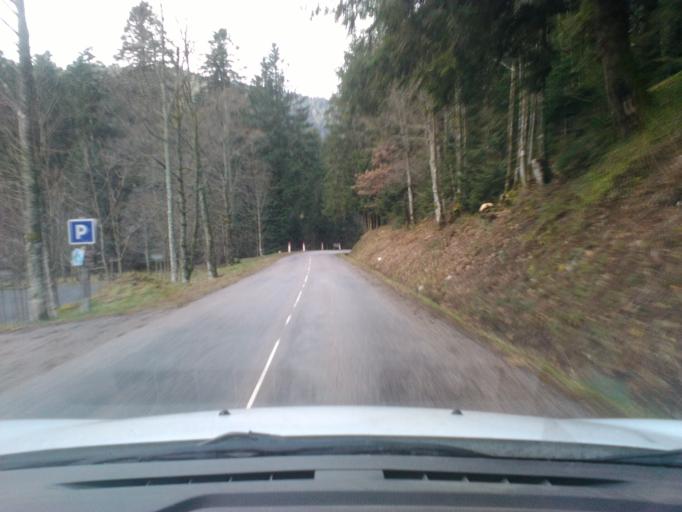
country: FR
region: Lorraine
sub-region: Departement des Vosges
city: Xonrupt-Longemer
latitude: 48.1161
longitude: 6.9579
